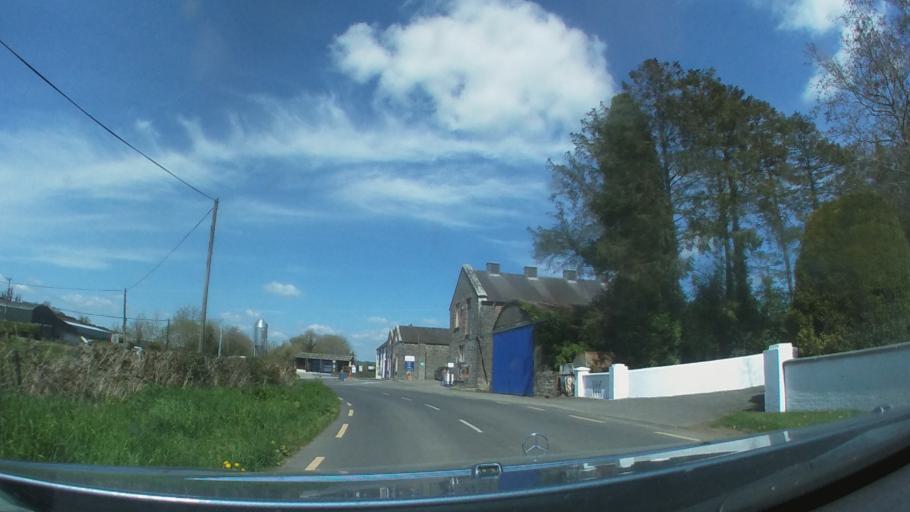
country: IE
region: Leinster
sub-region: Kilkenny
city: Callan
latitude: 52.6200
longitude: -7.4179
